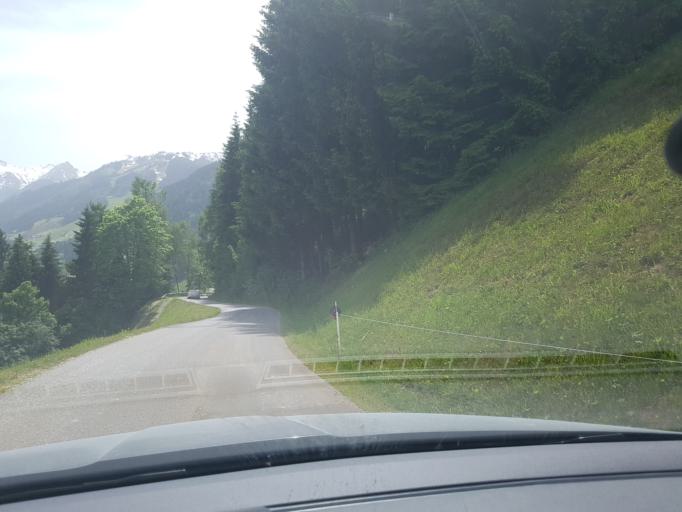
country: AT
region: Salzburg
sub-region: Politischer Bezirk Sankt Johann im Pongau
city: Schwarzach im Pongau
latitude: 47.2741
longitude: 13.2063
